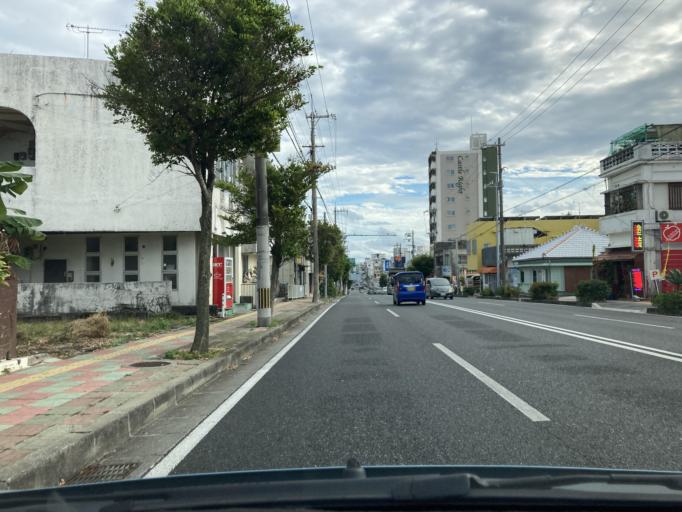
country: JP
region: Okinawa
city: Okinawa
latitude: 26.3421
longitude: 127.8140
